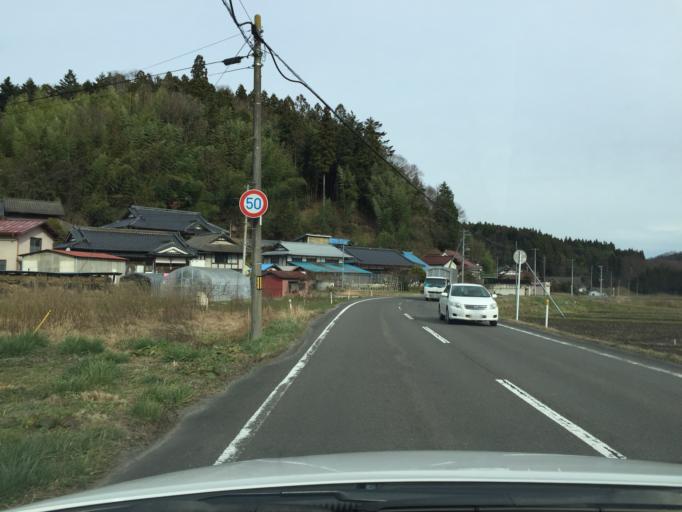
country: JP
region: Fukushima
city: Ishikawa
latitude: 37.2173
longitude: 140.6272
